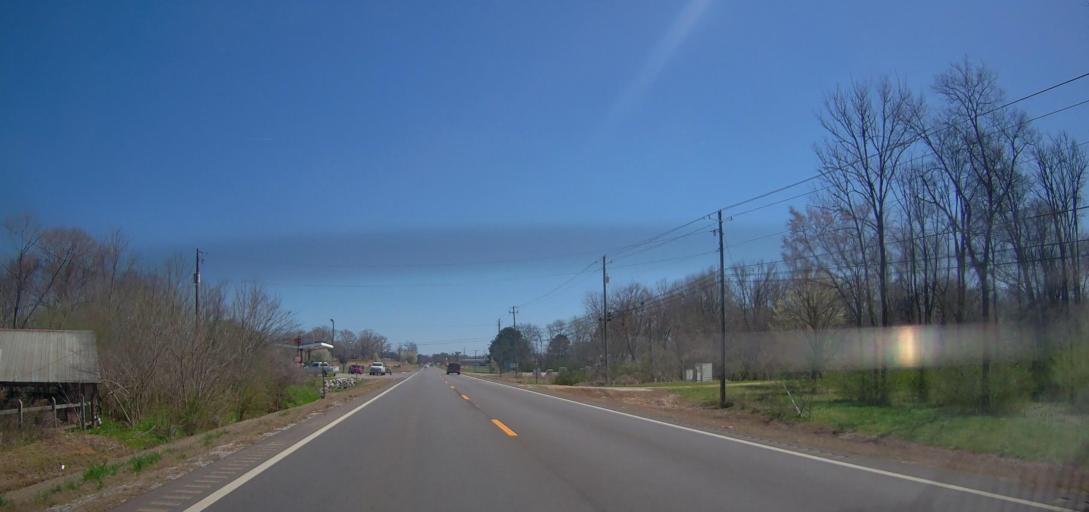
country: US
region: Alabama
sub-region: Calhoun County
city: Alexandria
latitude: 33.7825
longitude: -85.9063
